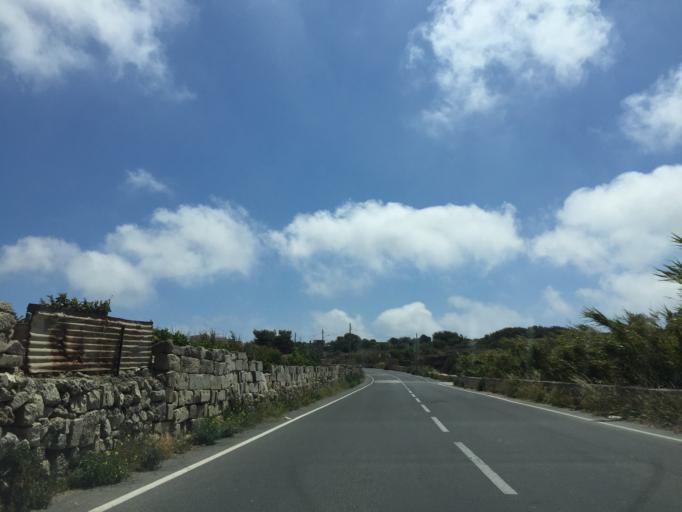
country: MT
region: Dingli
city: Dingli
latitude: 35.8672
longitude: 14.3904
